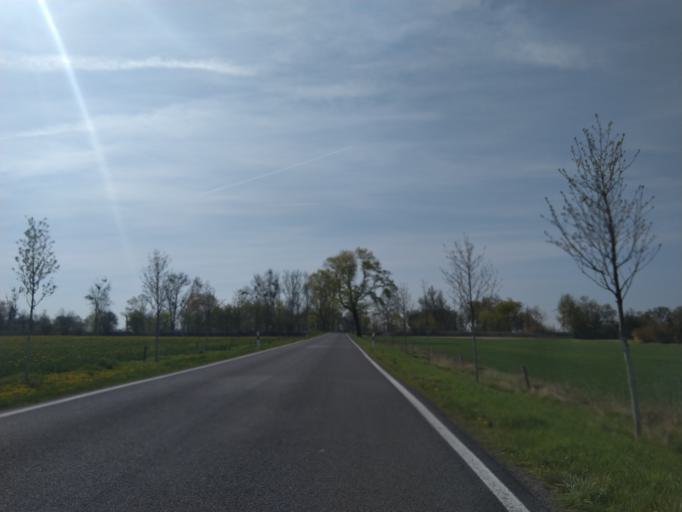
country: DE
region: Brandenburg
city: Bliesdorf
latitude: 52.7254
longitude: 14.1708
